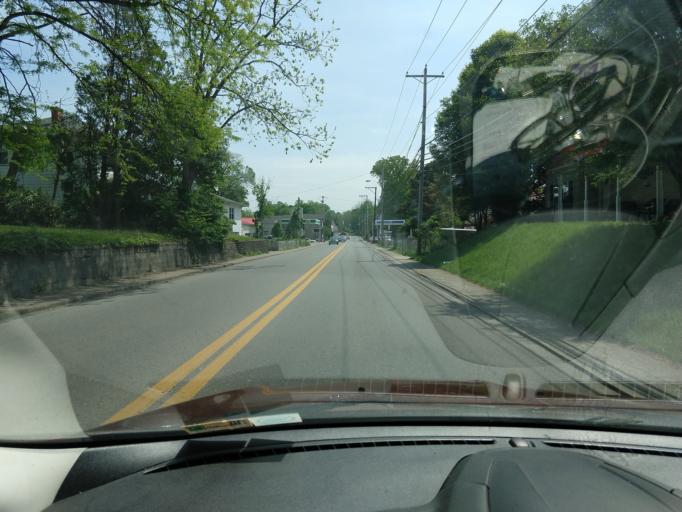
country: US
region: West Virginia
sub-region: Kanawha County
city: Saint Albans
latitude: 38.3775
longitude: -81.8088
